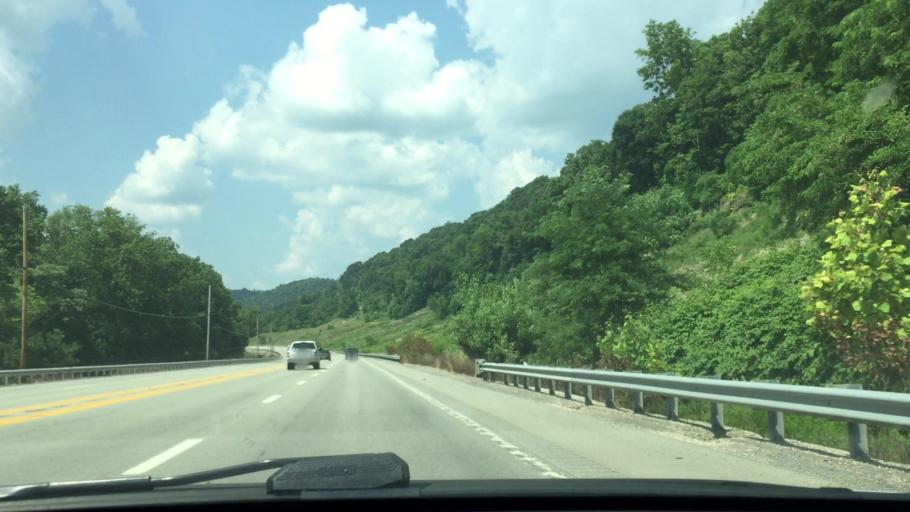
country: US
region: Ohio
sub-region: Belmont County
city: Powhatan Point
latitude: 39.8745
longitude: -80.7847
